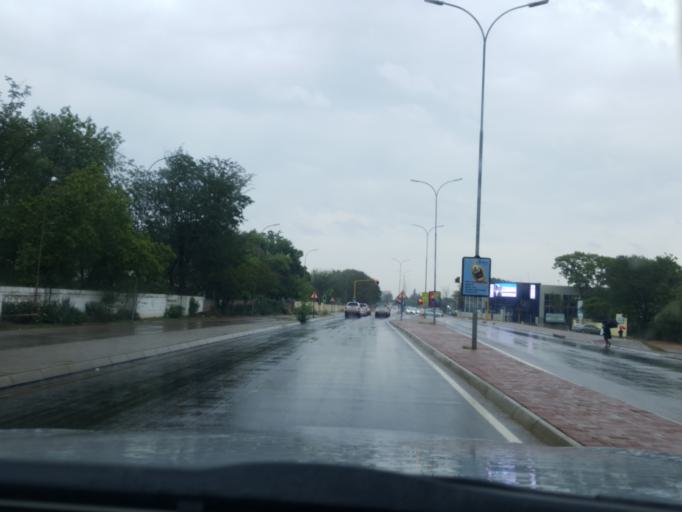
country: BW
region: South East
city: Gaborone
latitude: -24.6433
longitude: 25.9224
